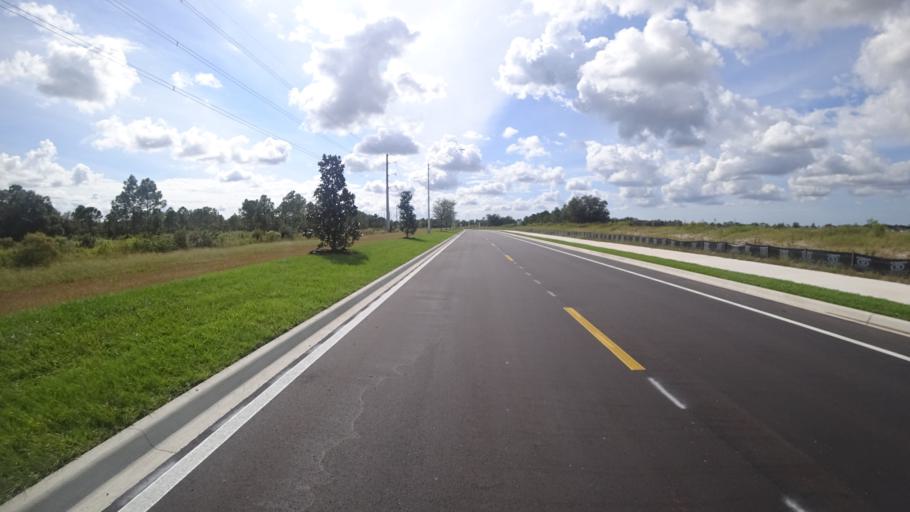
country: US
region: Florida
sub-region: Sarasota County
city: The Meadows
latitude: 27.4046
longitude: -82.3542
